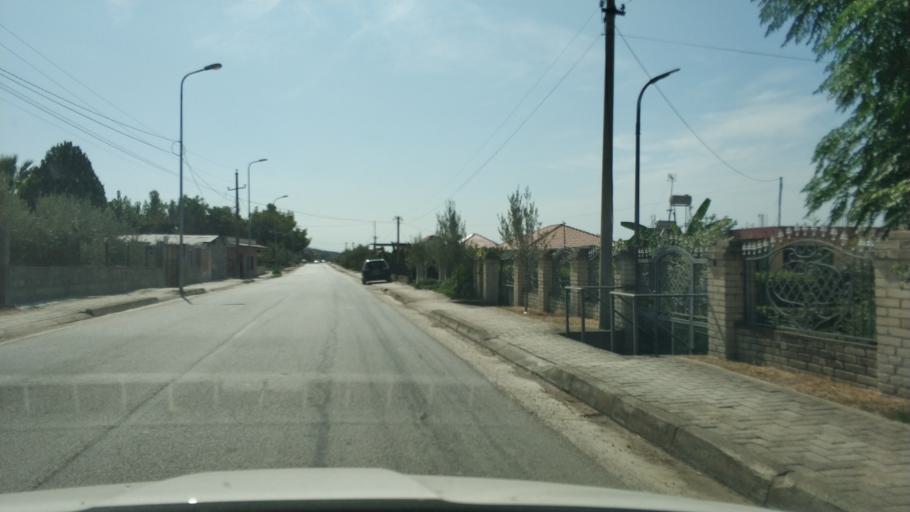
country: AL
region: Fier
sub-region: Rrethi i Lushnjes
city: Divjake
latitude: 40.9771
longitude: 19.5355
